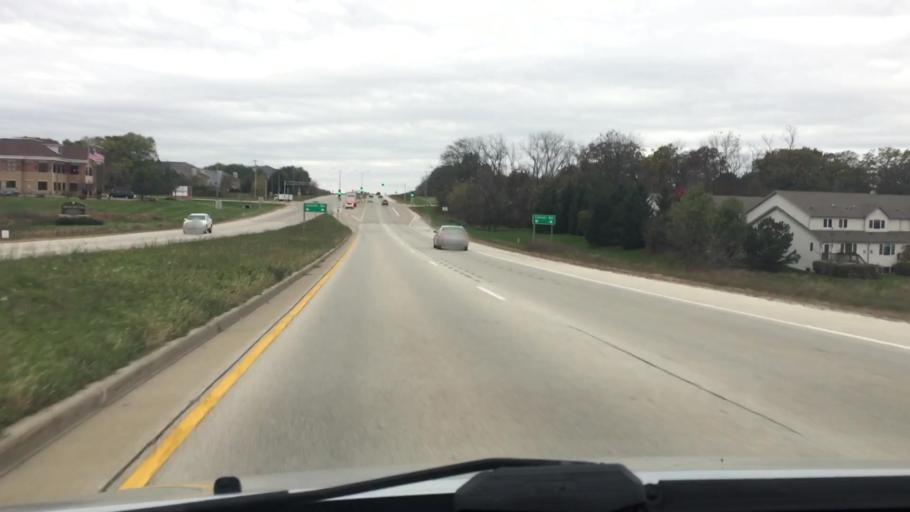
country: US
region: Wisconsin
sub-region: Waukesha County
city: Waukesha
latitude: 42.9770
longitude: -88.2442
